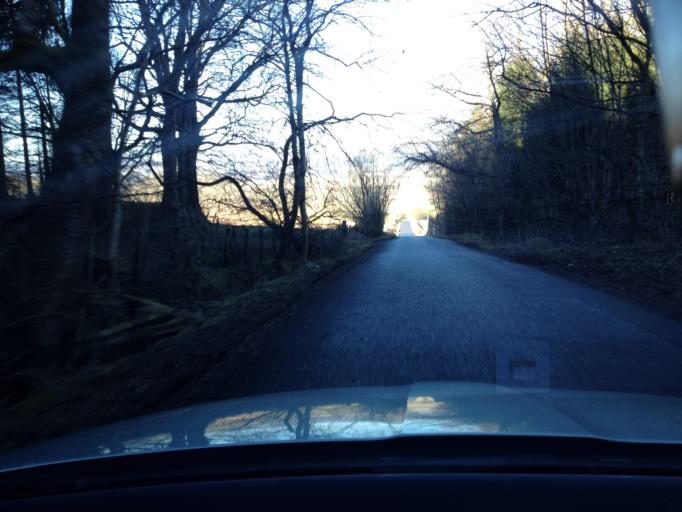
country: GB
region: Scotland
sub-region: Perth and Kinross
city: Bridge of Earn
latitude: 56.3186
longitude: -3.3705
